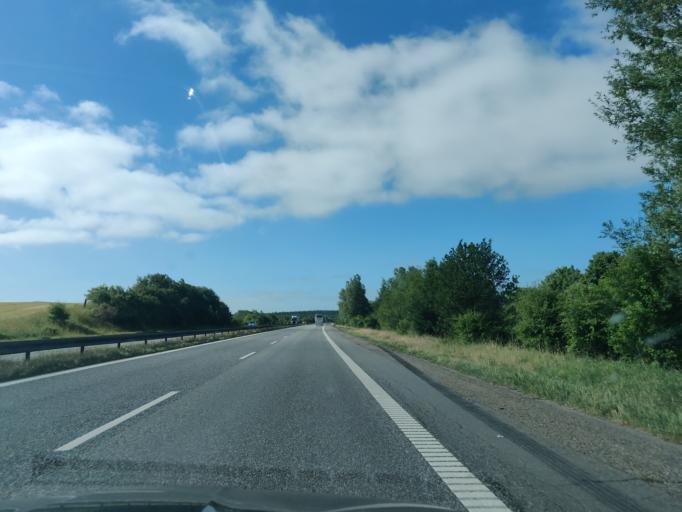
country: DK
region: North Denmark
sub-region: Mariagerfjord Kommune
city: Hobro
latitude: 56.6529
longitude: 9.7375
